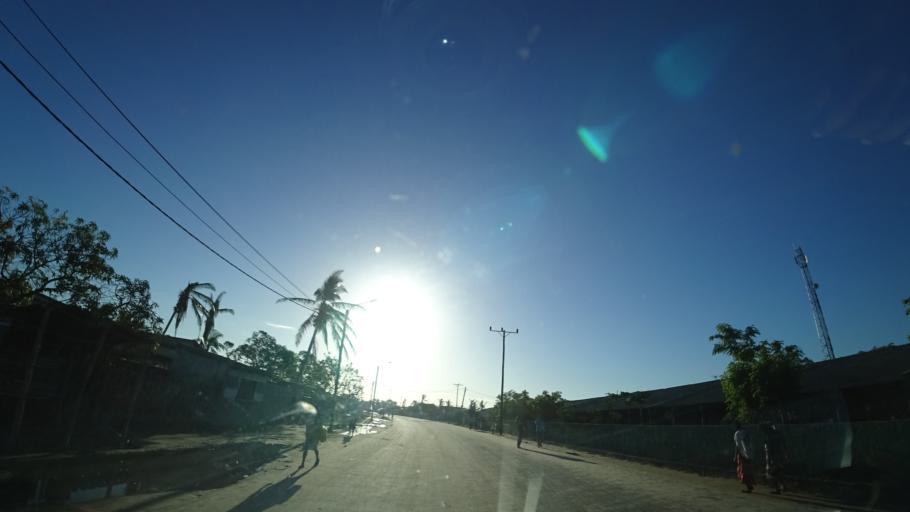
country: MZ
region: Sofala
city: Beira
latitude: -19.7439
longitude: 34.8436
